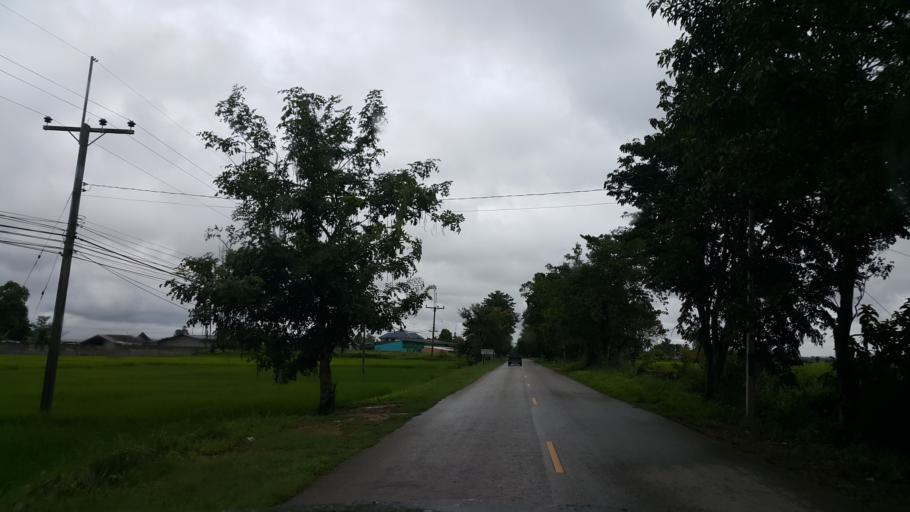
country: TH
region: Phayao
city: Chiang Kham
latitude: 19.5232
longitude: 100.3560
